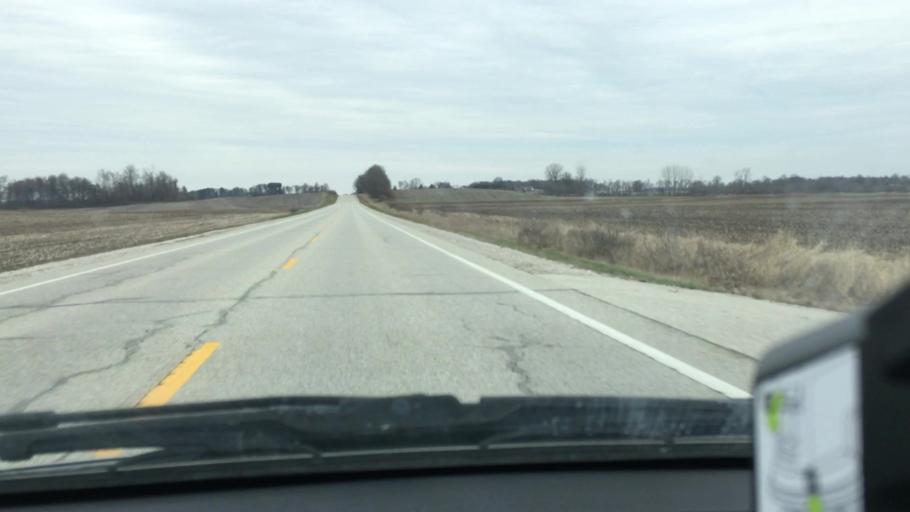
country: US
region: Indiana
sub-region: Daviess County
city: Odon
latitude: 38.9494
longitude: -87.0168
